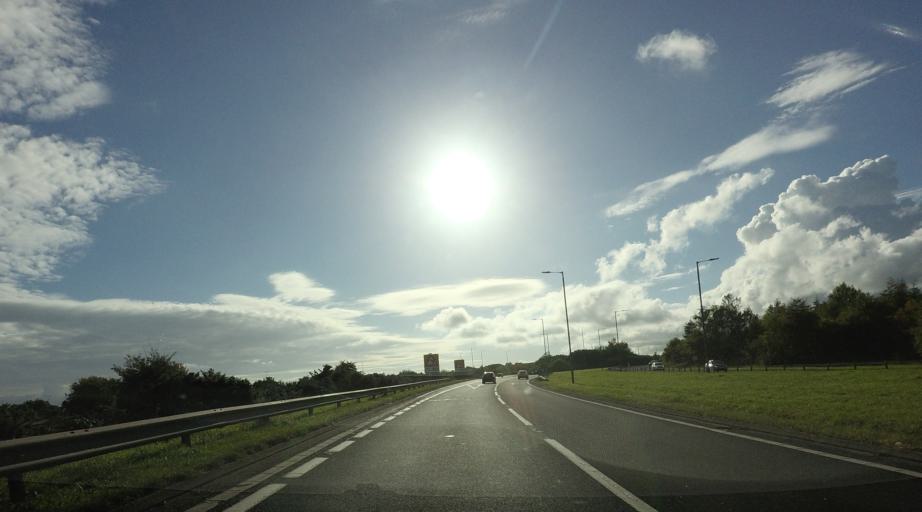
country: GB
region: Scotland
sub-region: Fife
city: Thornton
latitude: 56.1456
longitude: -3.1380
